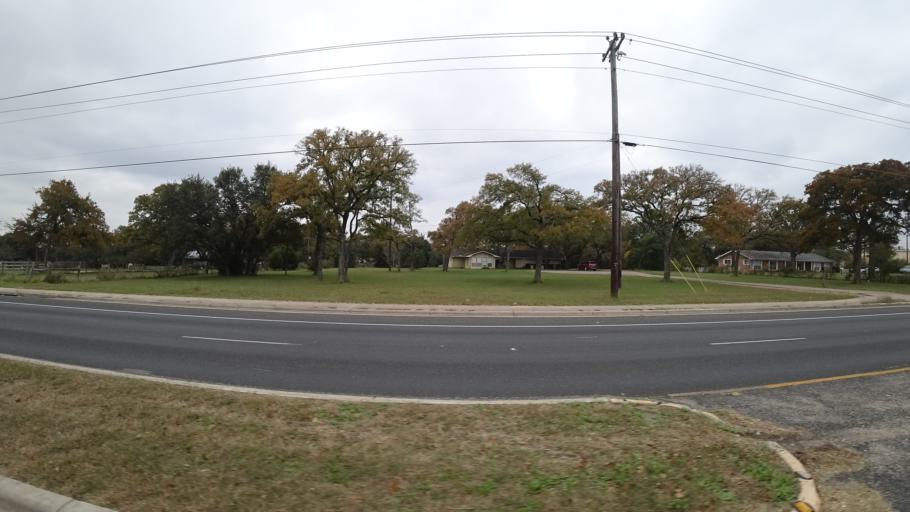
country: US
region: Texas
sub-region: Williamson County
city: Anderson Mill
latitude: 30.4534
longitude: -97.8231
